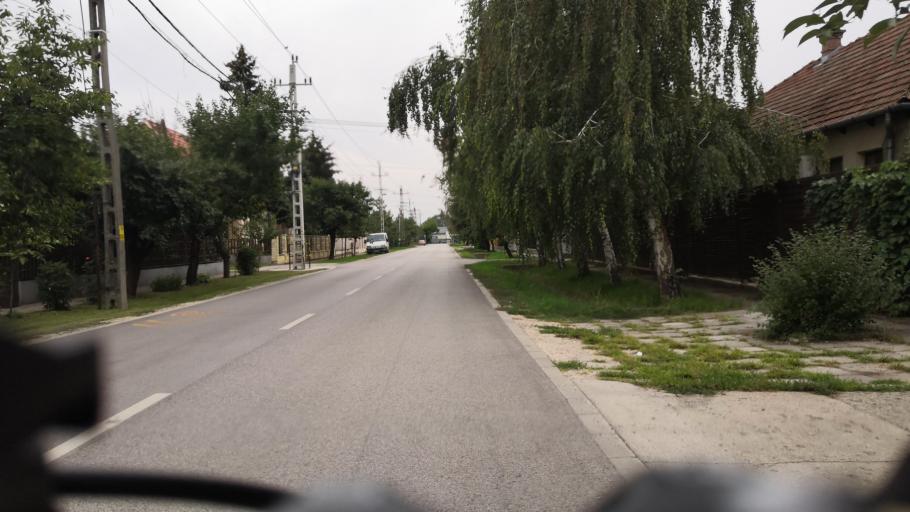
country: HU
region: Csongrad
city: Szeged
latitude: 46.2828
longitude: 20.1658
